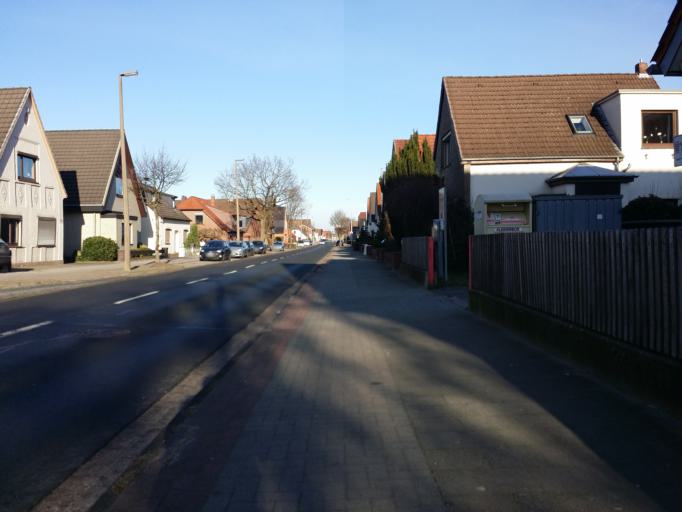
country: DE
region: Lower Saxony
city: Delmenhorst
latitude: 53.0427
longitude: 8.6543
